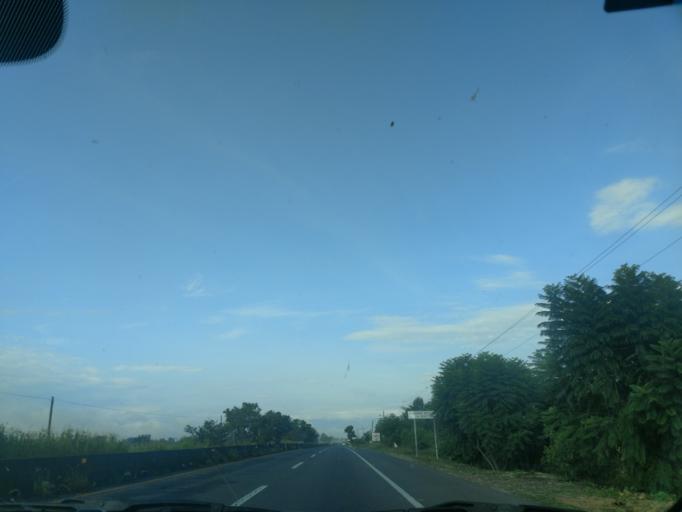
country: MX
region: Jalisco
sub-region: Ameca
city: Los Pocitos
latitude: 20.5480
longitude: -103.9044
